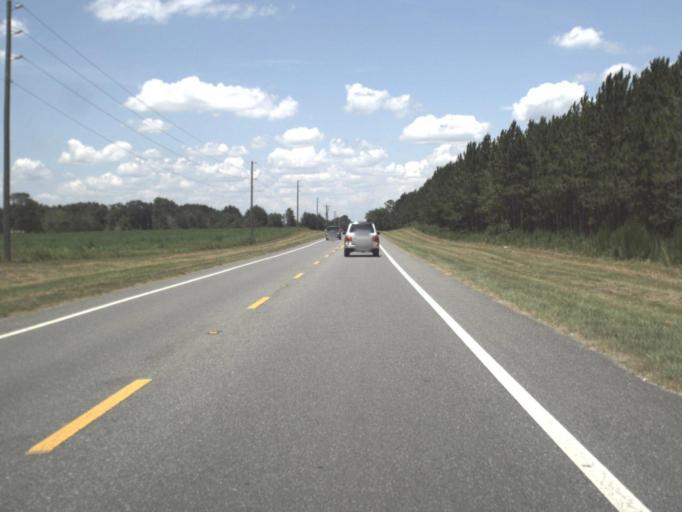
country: US
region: Florida
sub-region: Columbia County
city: Lake City
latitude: 30.0990
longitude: -82.7479
